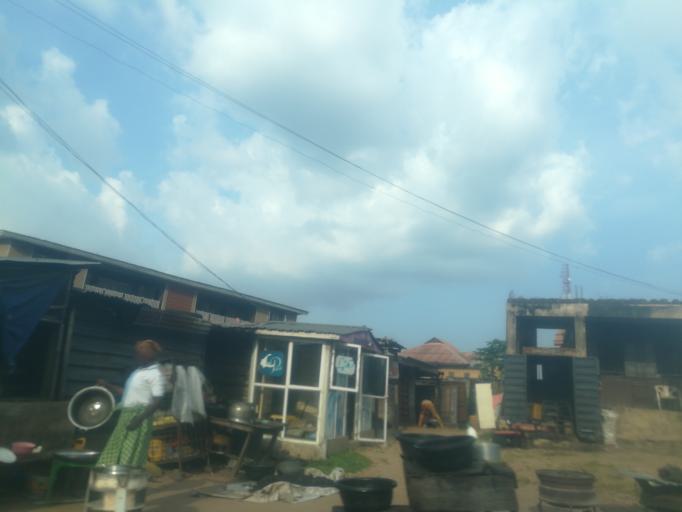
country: NG
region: Ogun
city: Abeokuta
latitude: 7.1416
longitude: 3.3301
